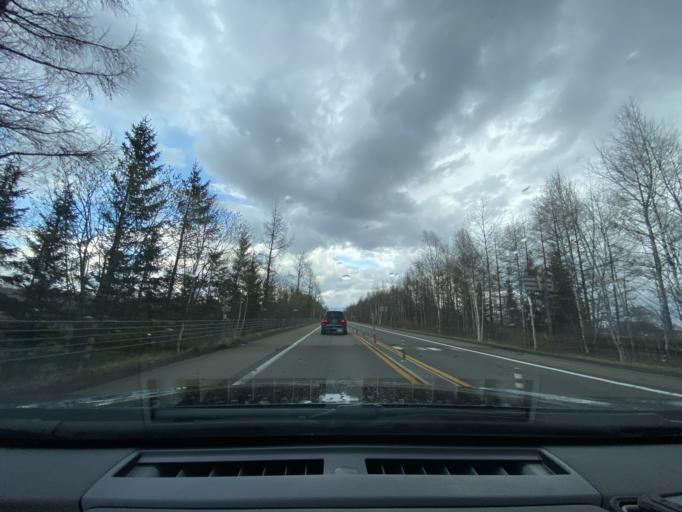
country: JP
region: Hokkaido
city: Otofuke
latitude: 42.9822
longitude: 142.9893
